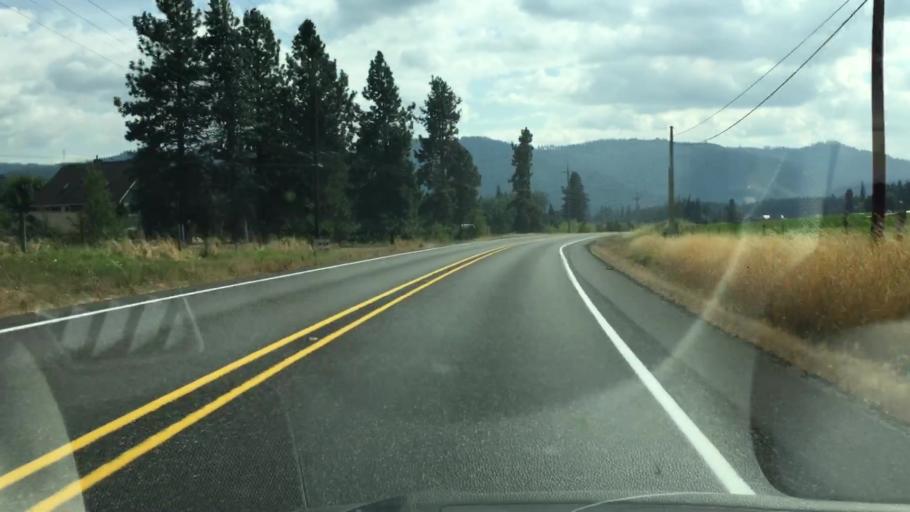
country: US
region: Washington
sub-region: Klickitat County
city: White Salmon
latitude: 45.8194
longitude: -121.4881
